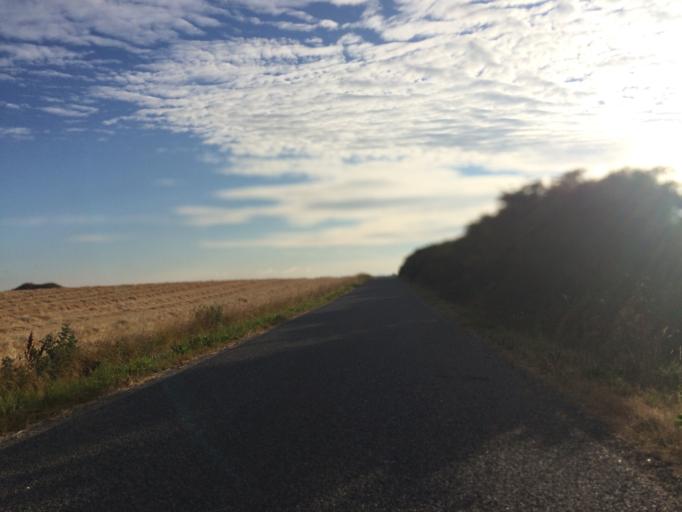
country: DK
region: Central Jutland
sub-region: Holstebro Kommune
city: Vinderup
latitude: 56.5906
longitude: 8.8278
